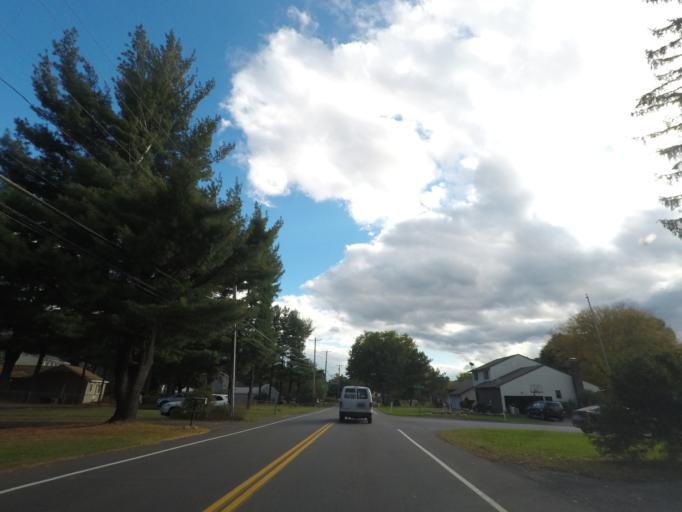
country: US
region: New York
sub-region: Schenectady County
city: Niskayuna
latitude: 42.7524
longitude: -73.8389
